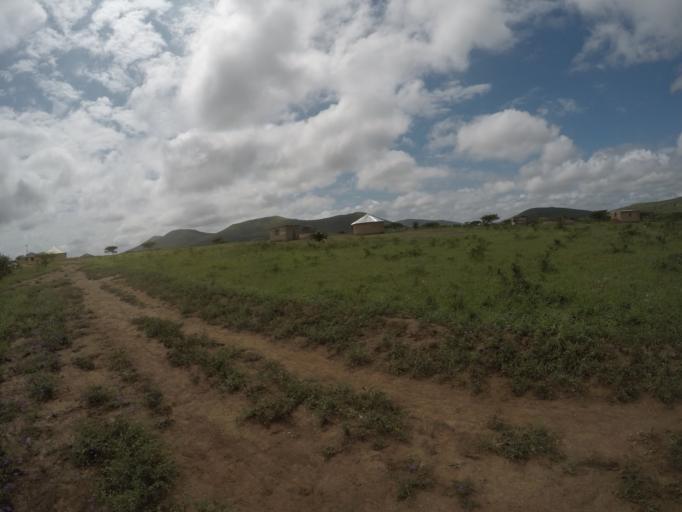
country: ZA
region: KwaZulu-Natal
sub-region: uThungulu District Municipality
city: Empangeni
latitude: -28.5848
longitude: 31.8522
